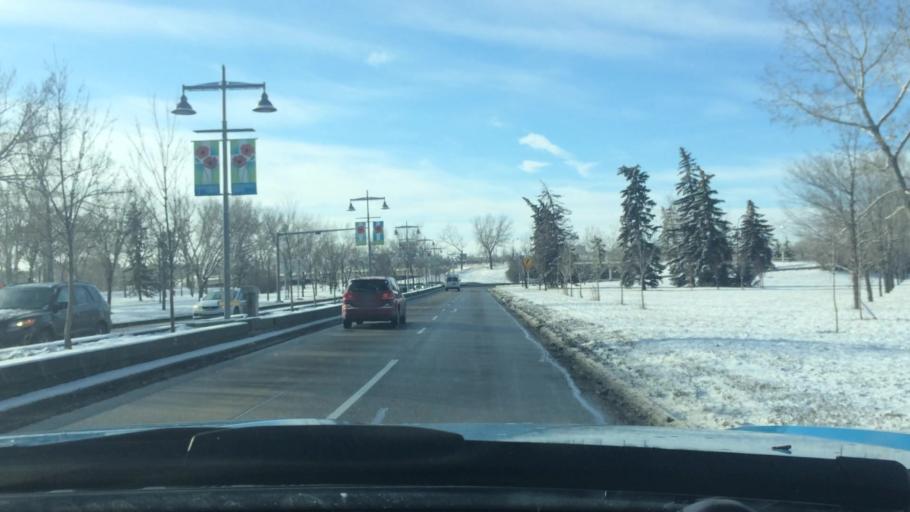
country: CA
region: Alberta
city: Calgary
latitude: 51.0506
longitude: -114.0920
